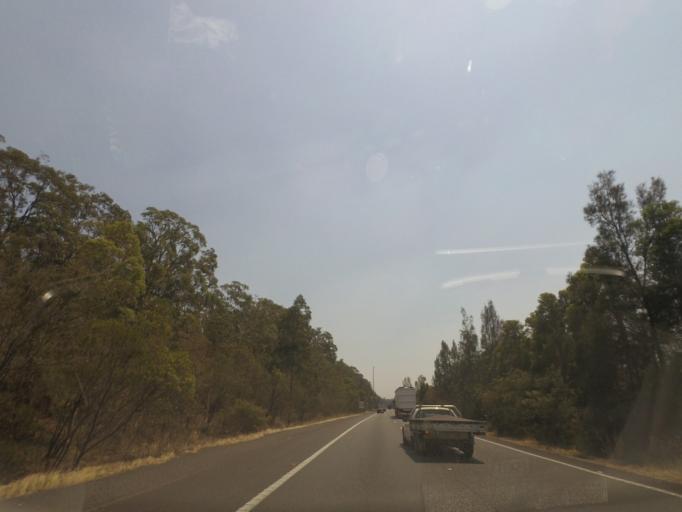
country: AU
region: New South Wales
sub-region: Newcastle
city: Beresfield
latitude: -32.8261
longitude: 151.6330
